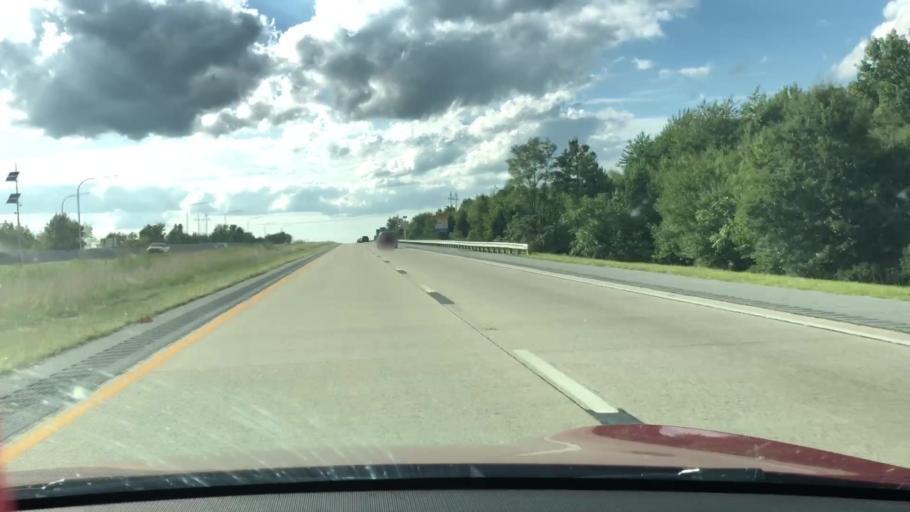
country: US
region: Delaware
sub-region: Kent County
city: Smyrna
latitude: 39.3273
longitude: -75.6191
